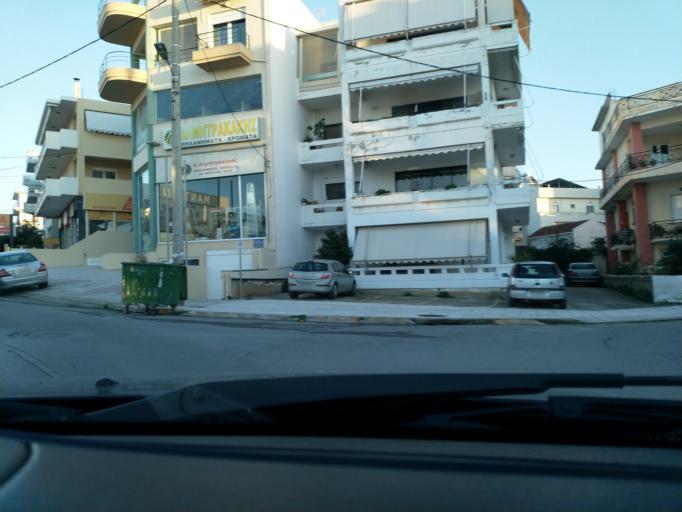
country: GR
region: Crete
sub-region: Nomos Chanias
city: Chania
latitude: 35.5099
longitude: 24.0099
